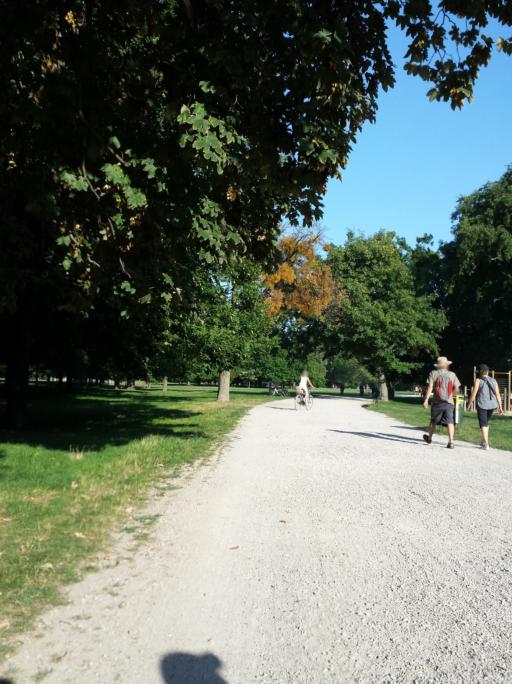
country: AT
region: Vienna
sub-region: Wien Stadt
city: Vienna
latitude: 48.2059
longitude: 16.4022
